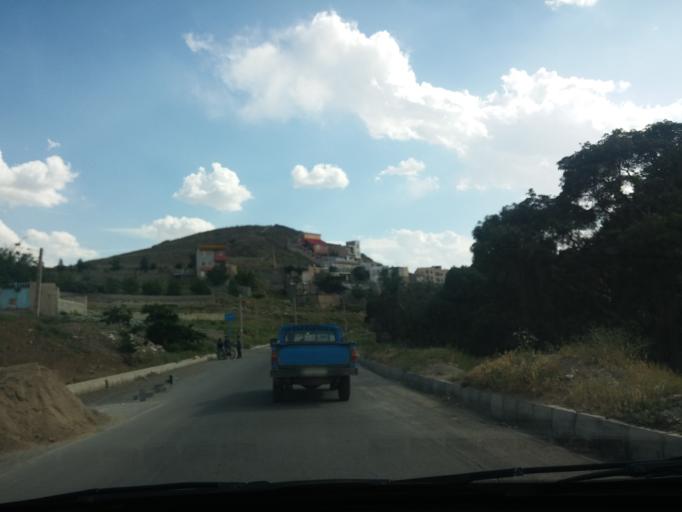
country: IR
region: Tehran
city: Damavand
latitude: 35.7288
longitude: 51.9057
